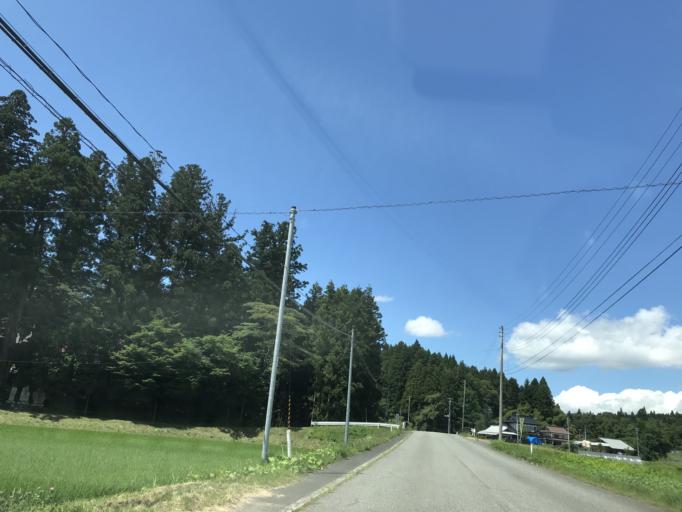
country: JP
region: Iwate
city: Ichinoseki
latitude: 38.9333
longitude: 141.0167
